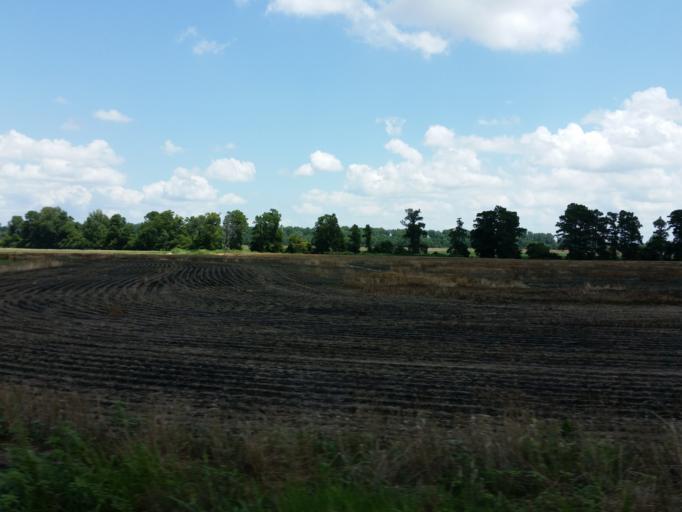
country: US
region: Kentucky
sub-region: Fulton County
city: Hickman
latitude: 36.5548
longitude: -89.2786
